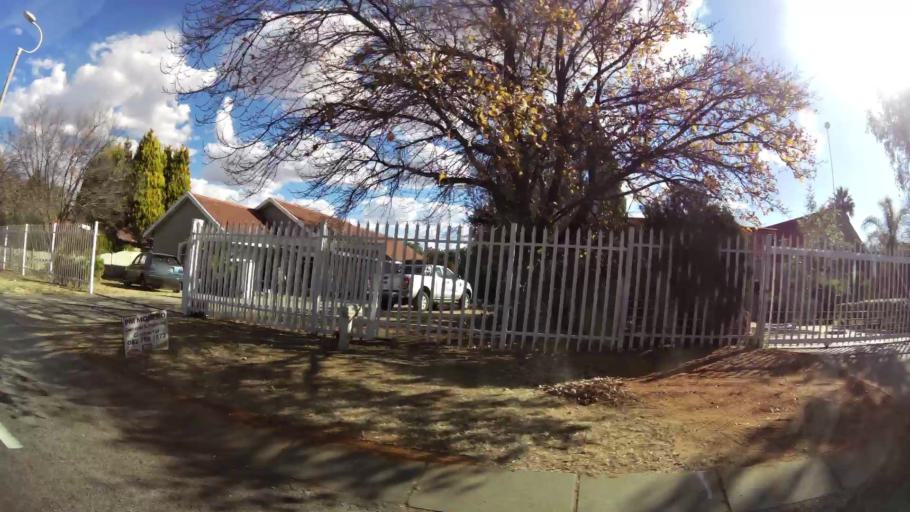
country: ZA
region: North-West
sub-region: Dr Kenneth Kaunda District Municipality
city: Klerksdorp
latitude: -26.8373
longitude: 26.6505
